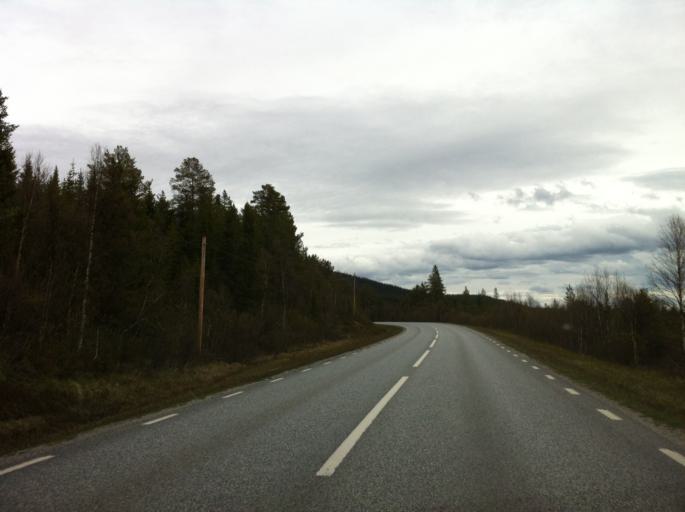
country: NO
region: Sor-Trondelag
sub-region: Tydal
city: Aas
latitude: 62.6132
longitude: 12.4973
